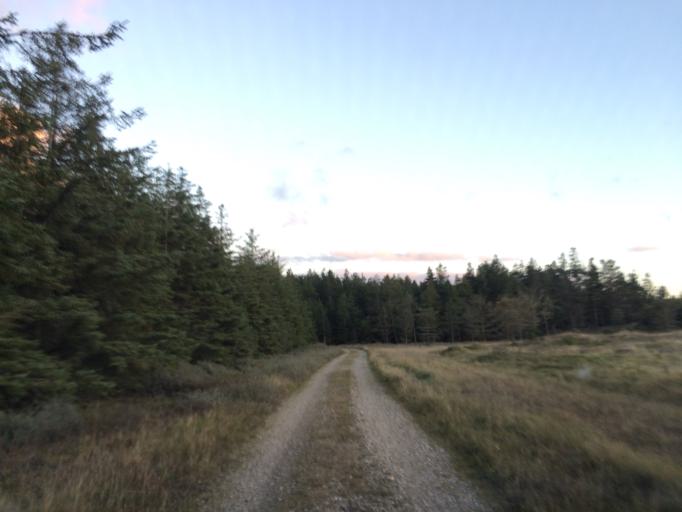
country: DK
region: Central Jutland
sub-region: Holstebro Kommune
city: Ulfborg
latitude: 56.2979
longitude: 8.1506
